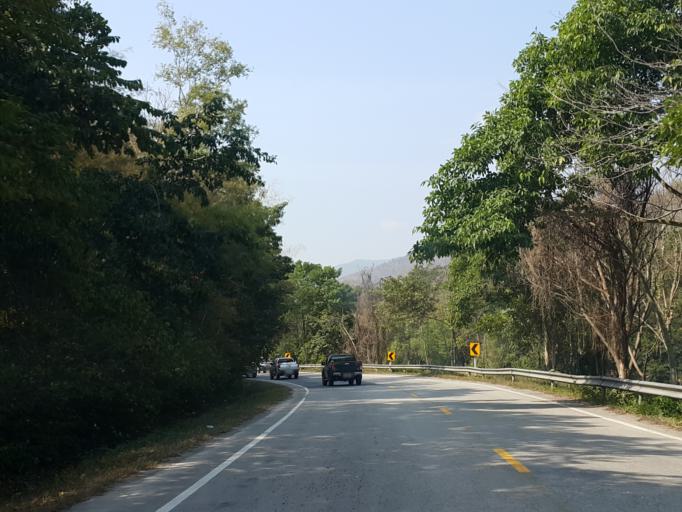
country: TH
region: Chiang Mai
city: Hot
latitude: 18.2343
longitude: 98.5464
